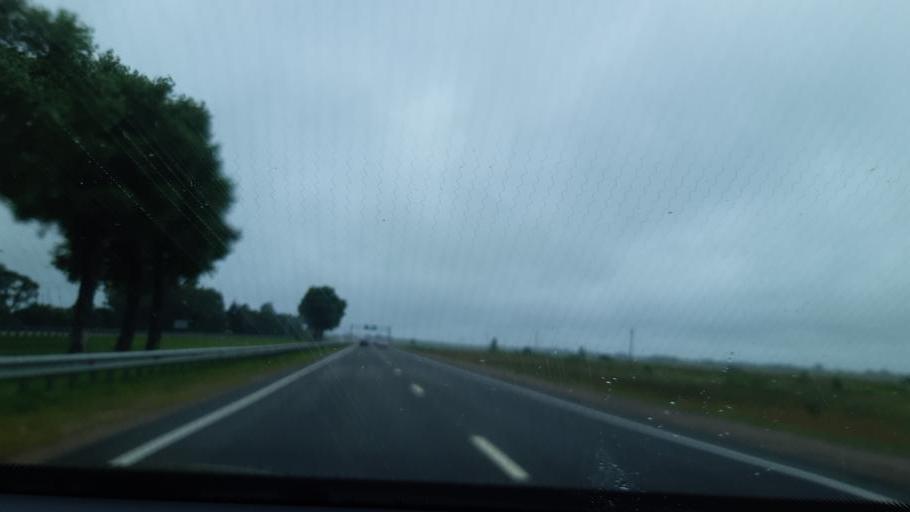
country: RU
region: Smolensk
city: Talashkino
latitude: 54.6925
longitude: 32.1301
